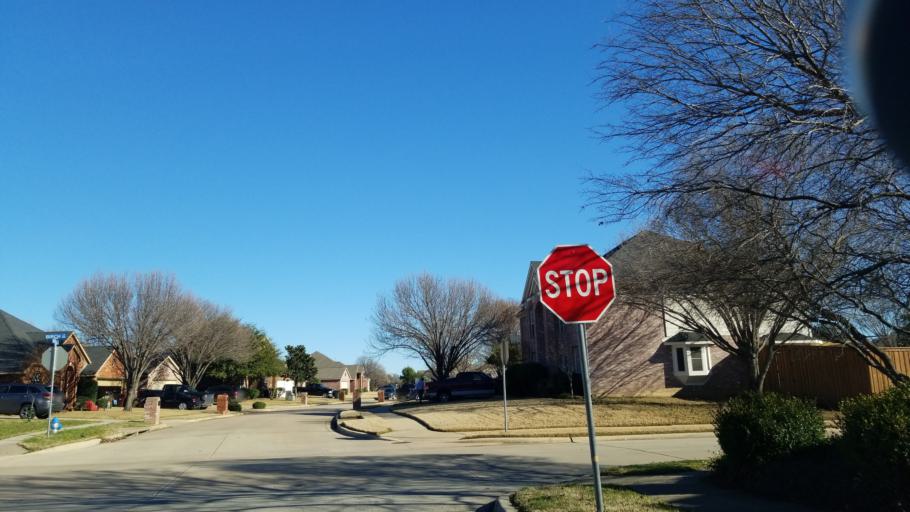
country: US
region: Texas
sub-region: Denton County
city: Corinth
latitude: 33.1386
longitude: -97.0857
